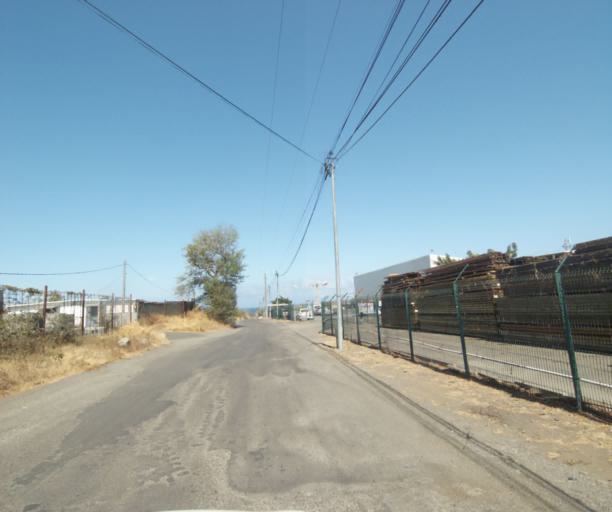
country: RE
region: Reunion
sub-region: Reunion
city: Le Port
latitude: -20.9638
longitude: 55.2882
